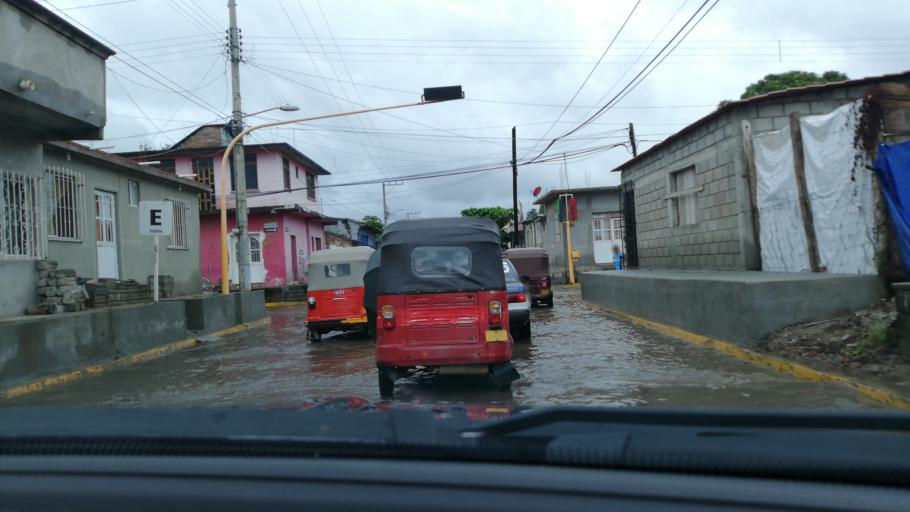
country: MX
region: Oaxaca
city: Juchitan de Zaragoza
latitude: 16.4341
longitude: -95.0177
